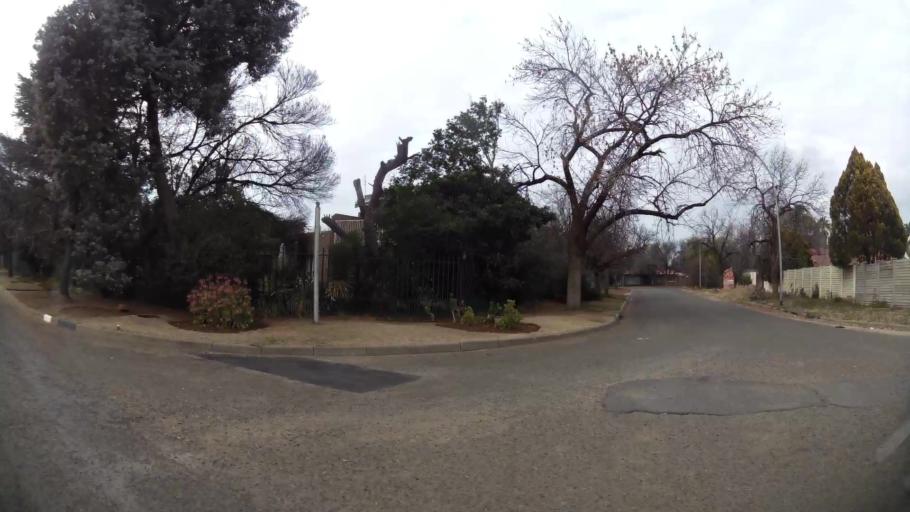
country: ZA
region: Orange Free State
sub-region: Mangaung Metropolitan Municipality
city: Bloemfontein
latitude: -29.1242
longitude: 26.1856
